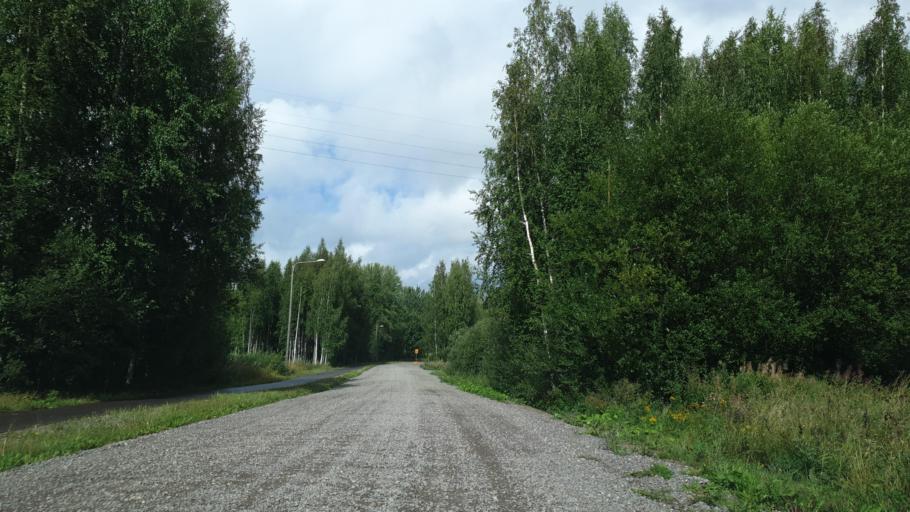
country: FI
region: Northern Savo
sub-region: Varkaus
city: Varkaus
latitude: 62.3389
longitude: 27.8544
